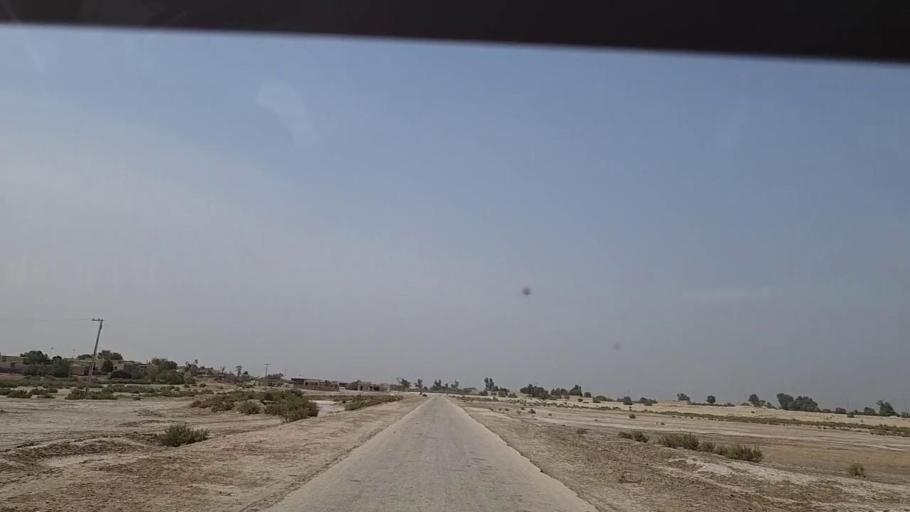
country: PK
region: Sindh
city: Khairpur Nathan Shah
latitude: 27.0705
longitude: 67.6512
